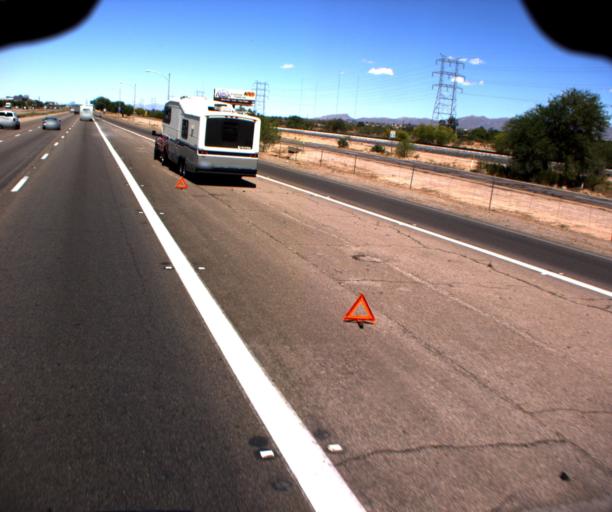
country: US
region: Arizona
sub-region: Pima County
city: Flowing Wells
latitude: 32.3406
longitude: -111.0694
